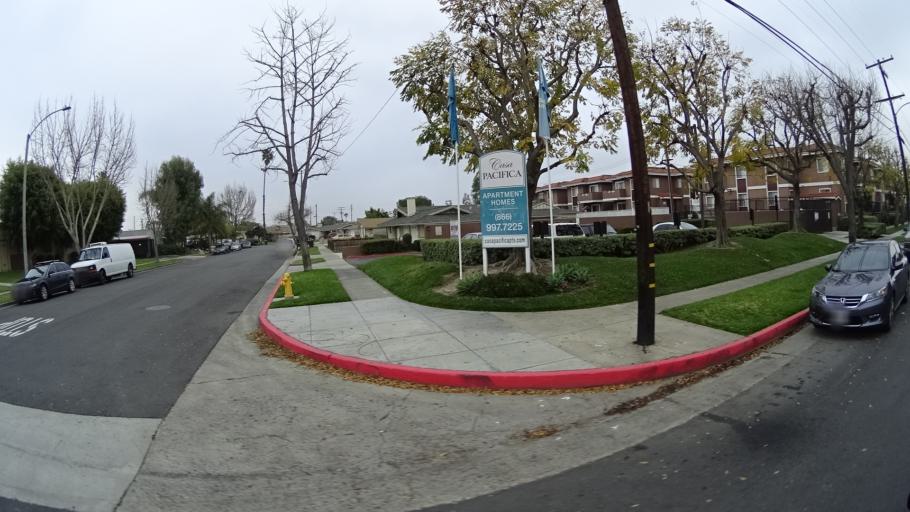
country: US
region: California
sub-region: Orange County
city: Cypress
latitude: 33.8198
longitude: -118.0138
